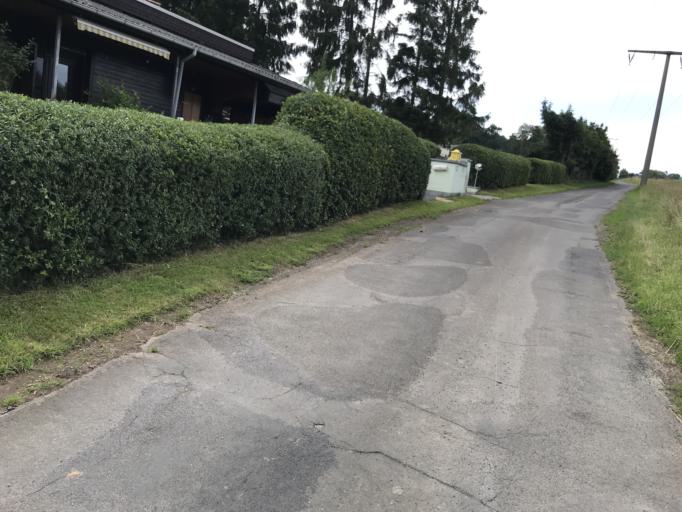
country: DE
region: Hesse
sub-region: Regierungsbezirk Giessen
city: Laubach
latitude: 50.5240
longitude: 8.9688
